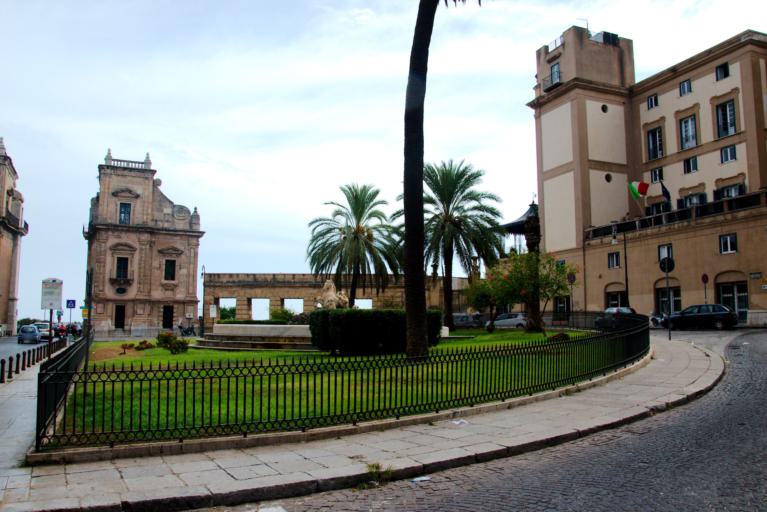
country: IT
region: Sicily
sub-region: Palermo
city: Palermo
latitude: 38.1194
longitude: 13.3704
